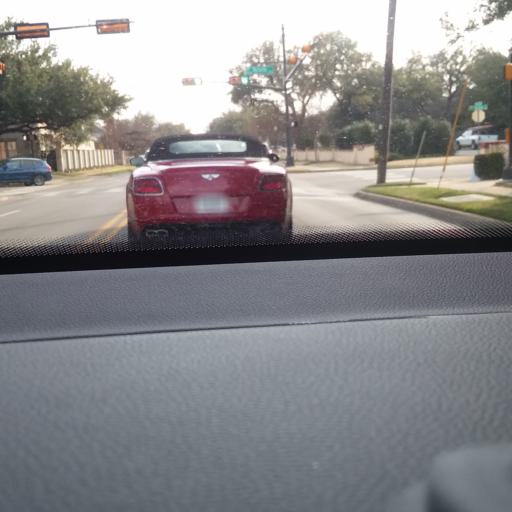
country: US
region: Texas
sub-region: Dallas County
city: University Park
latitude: 32.8444
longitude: -96.8043
